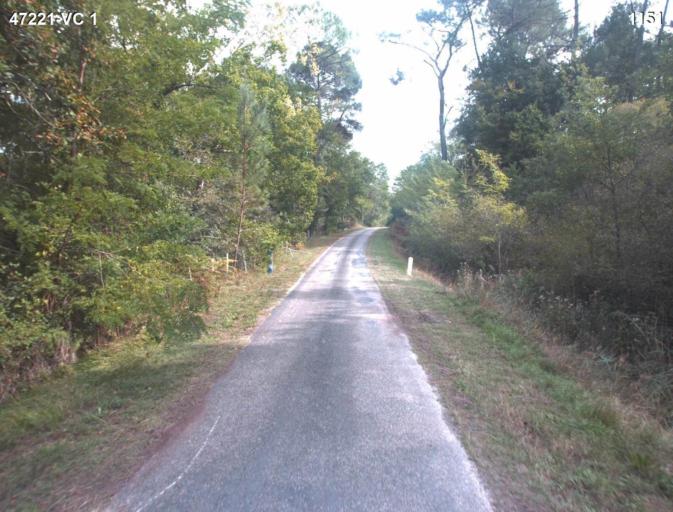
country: FR
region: Aquitaine
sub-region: Departement du Lot-et-Garonne
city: Mezin
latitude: 44.1109
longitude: 0.2310
